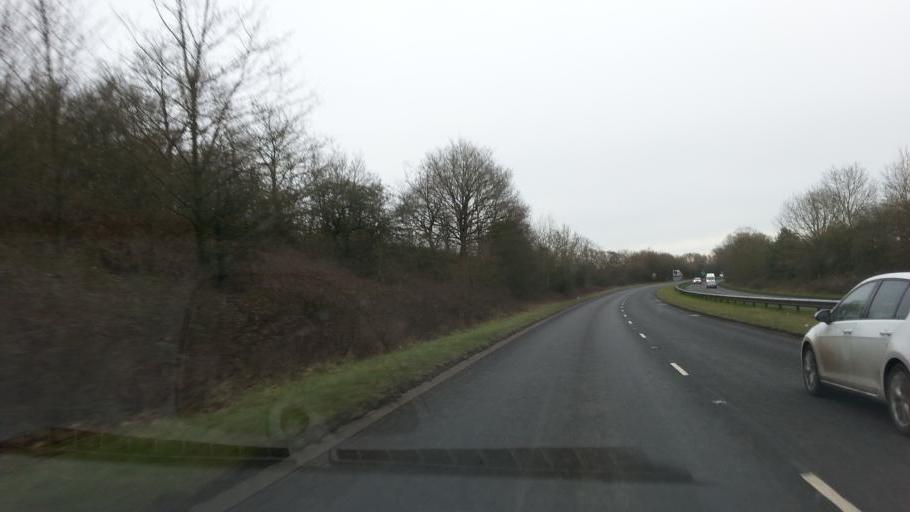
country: GB
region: England
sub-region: Solihull
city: Tidbury Green
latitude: 52.3796
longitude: -1.8903
